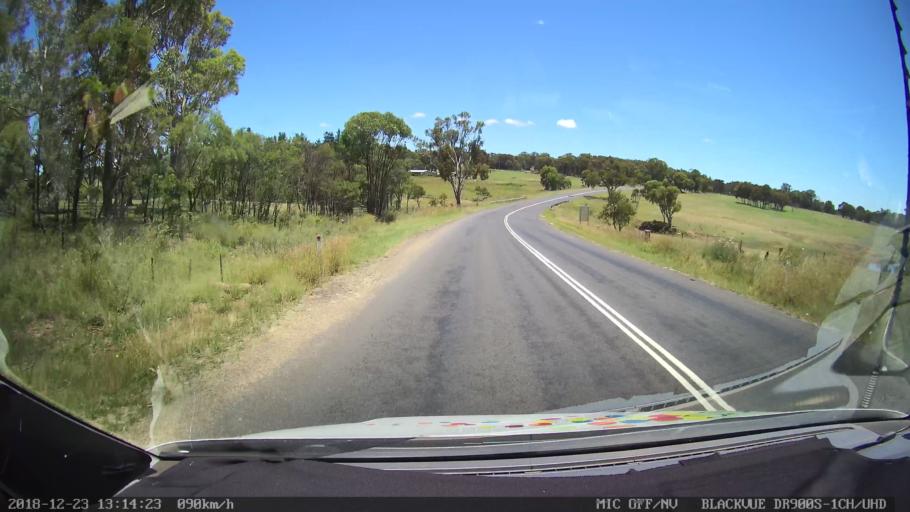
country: AU
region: New South Wales
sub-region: Armidale Dumaresq
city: Armidale
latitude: -30.5037
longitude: 151.5282
